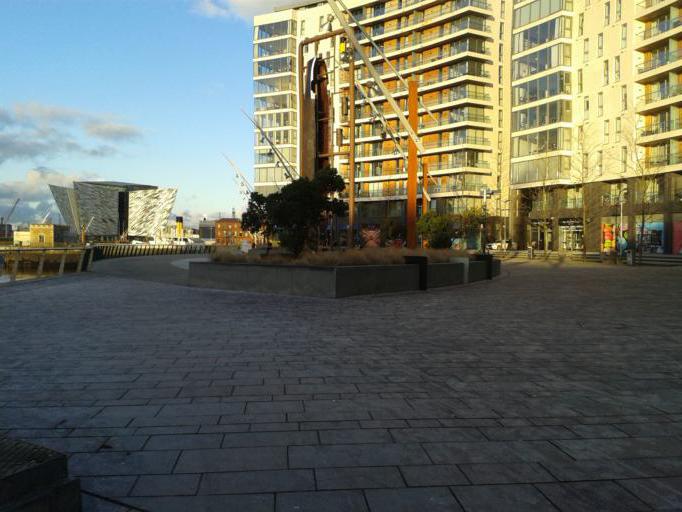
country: GB
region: Northern Ireland
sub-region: City of Belfast
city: Belfast
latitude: 54.6046
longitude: -5.9130
